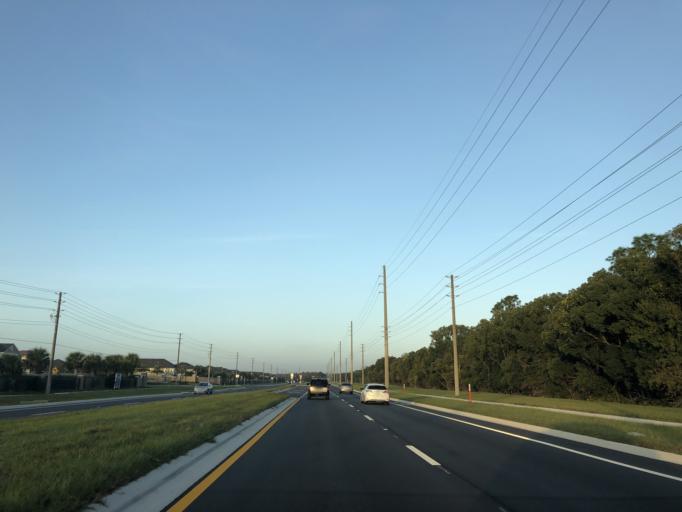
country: US
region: Florida
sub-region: Osceola County
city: Kissimmee
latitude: 28.3248
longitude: -81.4293
